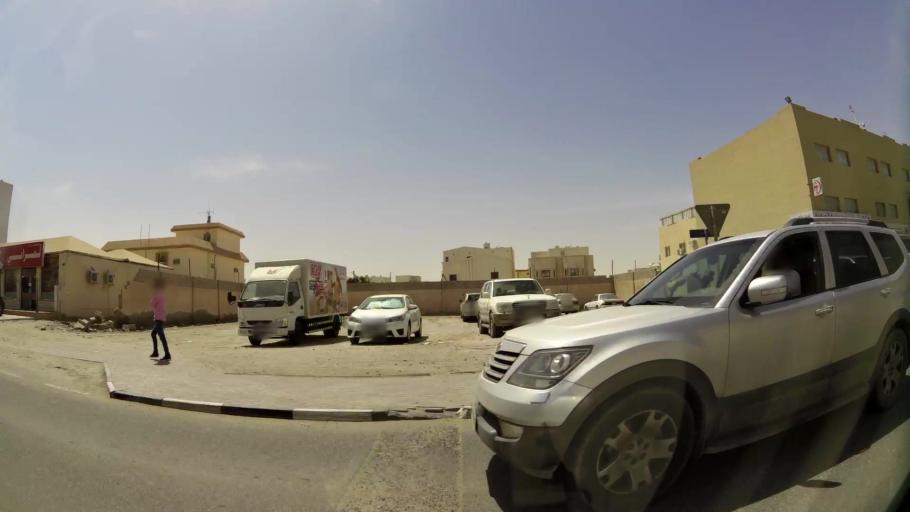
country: QA
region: Baladiyat ar Rayyan
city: Ar Rayyan
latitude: 25.2713
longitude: 51.4082
